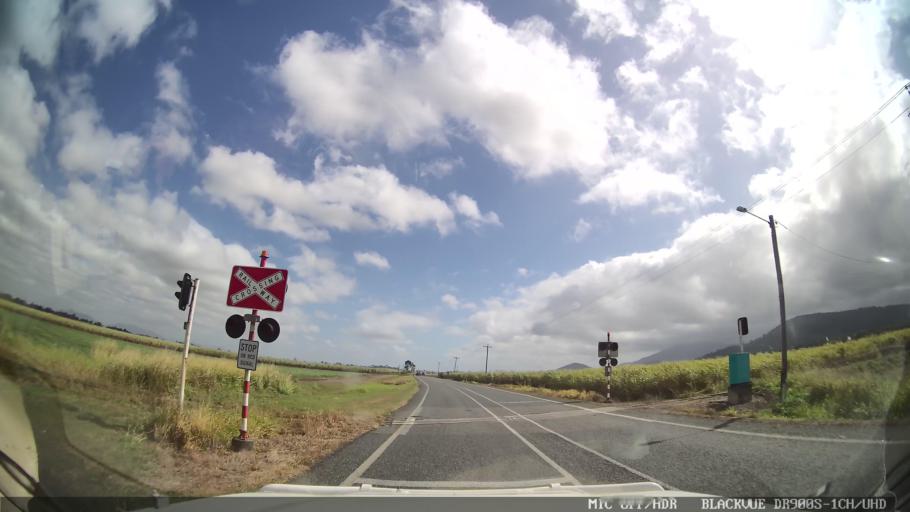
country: AU
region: Queensland
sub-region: Whitsunday
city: Proserpine
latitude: -20.3485
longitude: 148.5547
